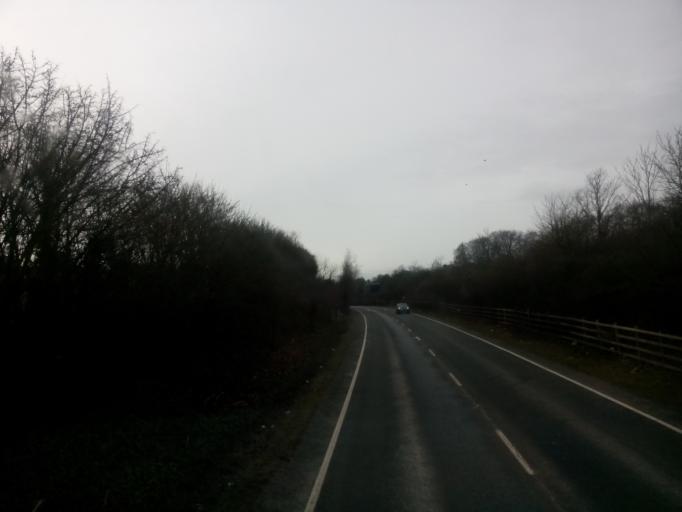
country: GB
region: England
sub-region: Hampshire
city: Kings Worthy
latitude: 51.0665
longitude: -1.2920
